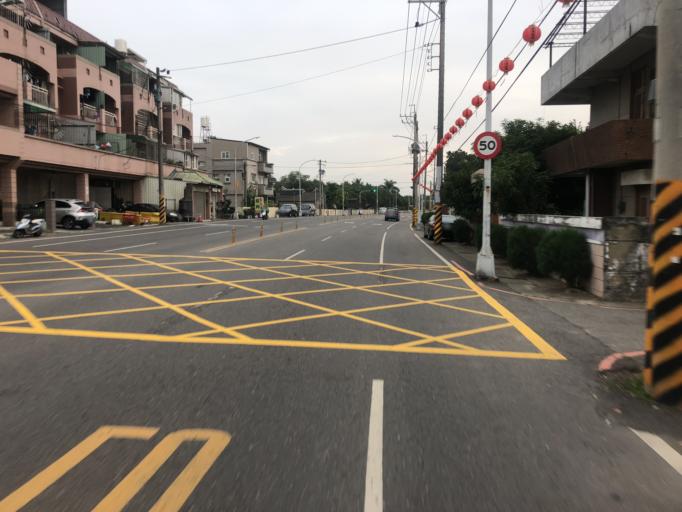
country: TW
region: Taiwan
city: Xinying
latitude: 23.1485
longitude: 120.2879
